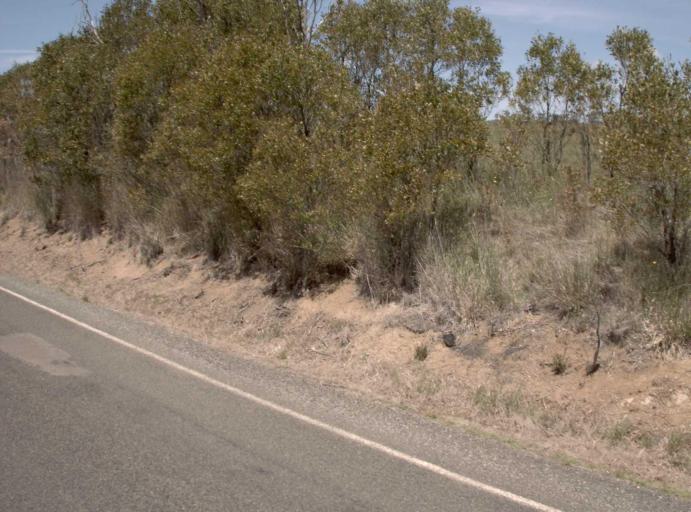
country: AU
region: Victoria
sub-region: Alpine
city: Mount Beauty
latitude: -37.1455
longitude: 147.6477
